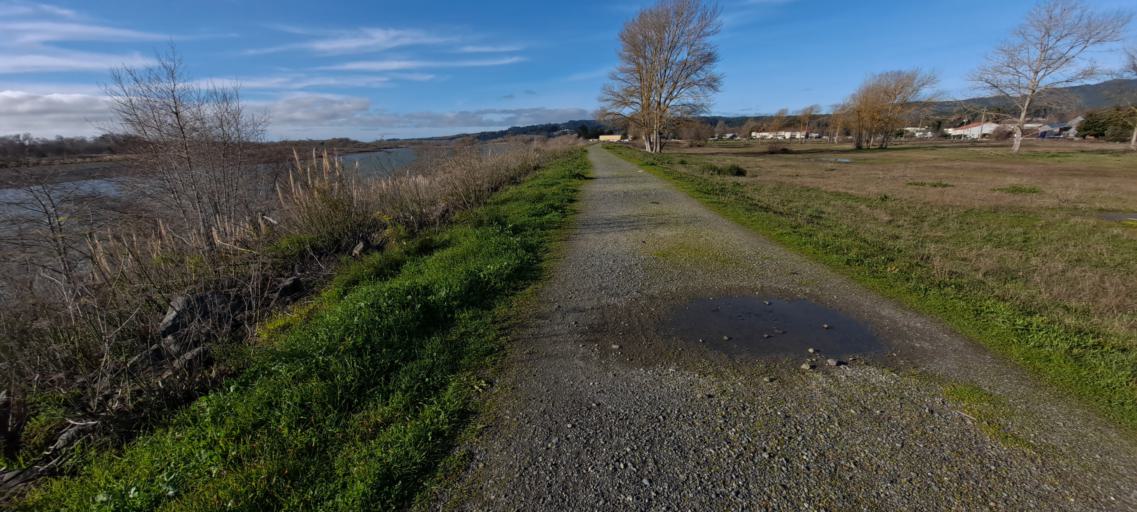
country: US
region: California
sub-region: Humboldt County
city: Fortuna
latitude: 40.5791
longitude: -124.1556
